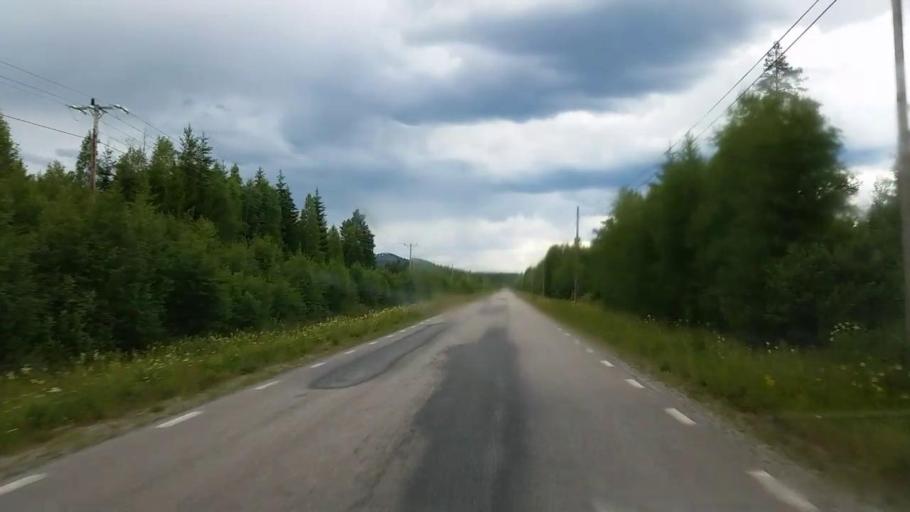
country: SE
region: Gaevleborg
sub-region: Ovanakers Kommun
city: Edsbyn
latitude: 61.4447
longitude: 15.8863
